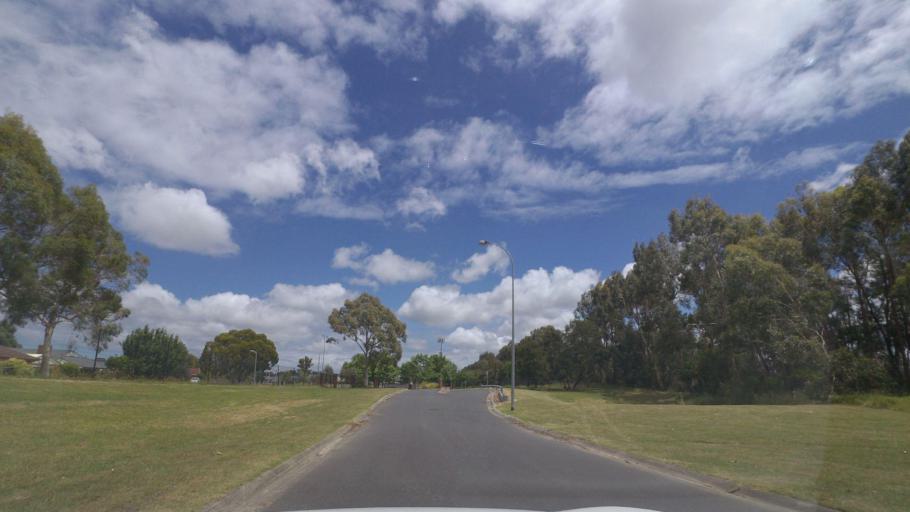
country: AU
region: Victoria
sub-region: Knox
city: Knoxfield
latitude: -37.9044
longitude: 145.2582
